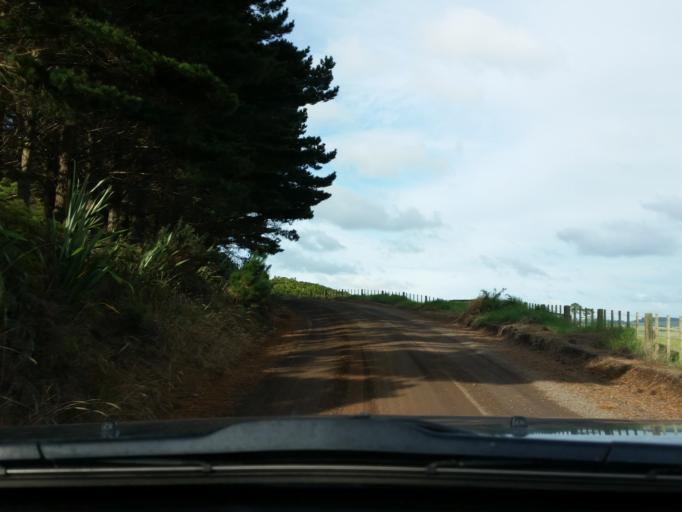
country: NZ
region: Northland
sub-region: Kaipara District
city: Dargaville
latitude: -35.7573
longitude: 173.6134
